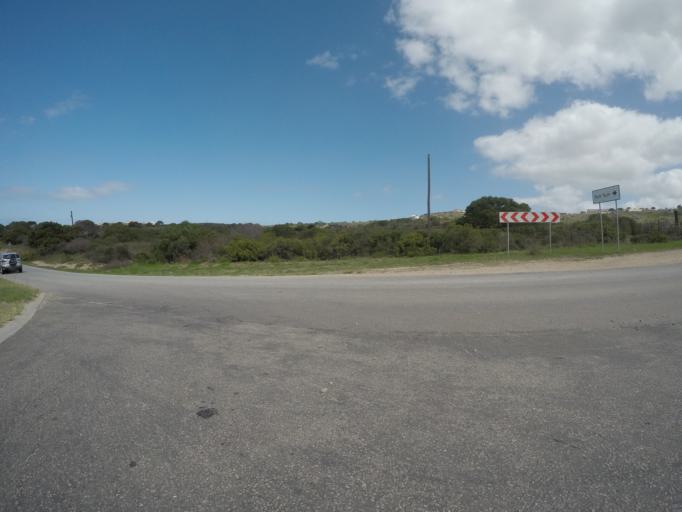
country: ZA
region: Western Cape
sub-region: Eden District Municipality
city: Mossel Bay
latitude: -34.1442
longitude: 22.0882
